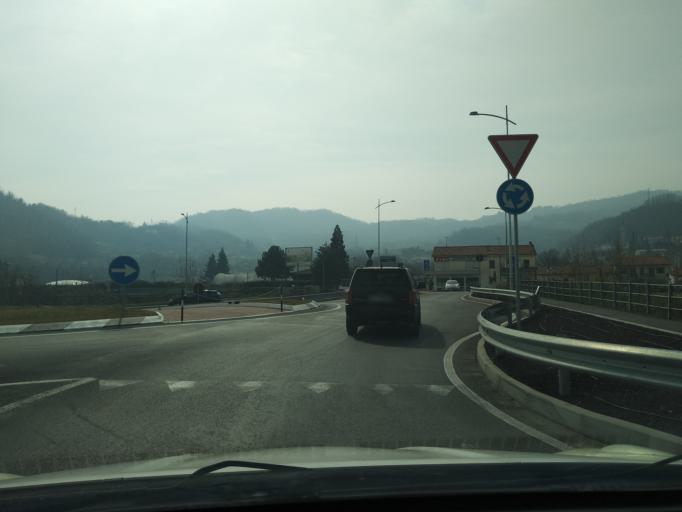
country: IT
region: Veneto
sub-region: Provincia di Vicenza
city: Arzignano
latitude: 45.5228
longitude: 11.3219
